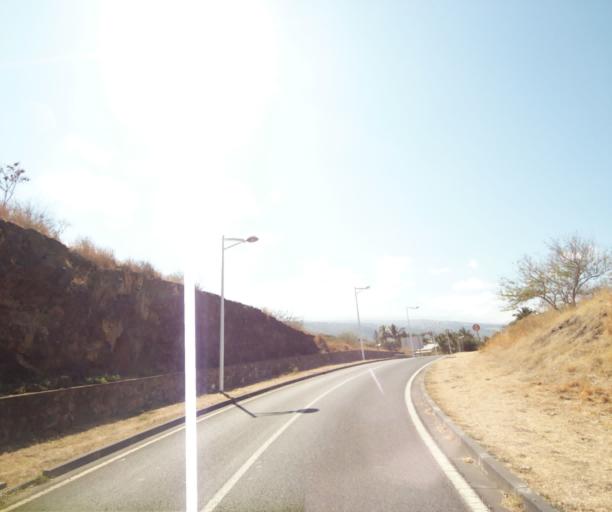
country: RE
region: Reunion
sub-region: Reunion
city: Trois-Bassins
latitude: -21.1029
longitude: 55.2484
